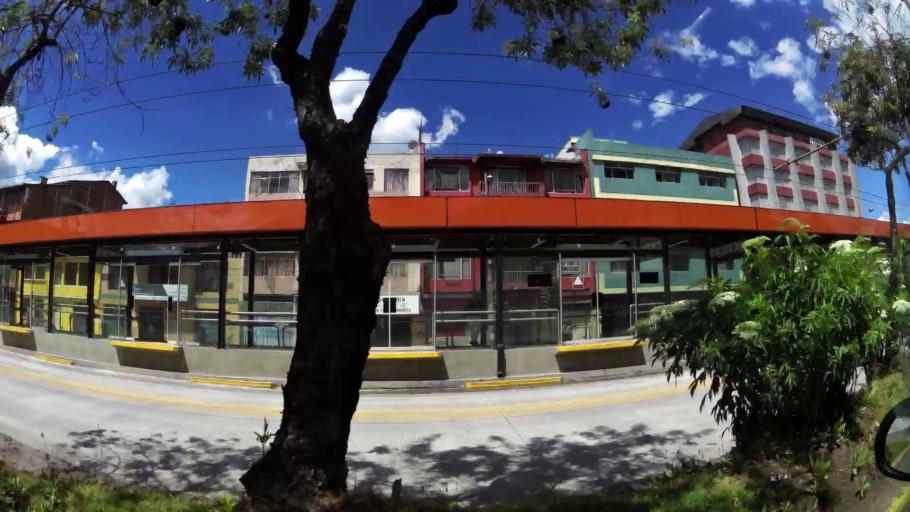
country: EC
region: Pichincha
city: Quito
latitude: -0.1874
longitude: -78.4916
